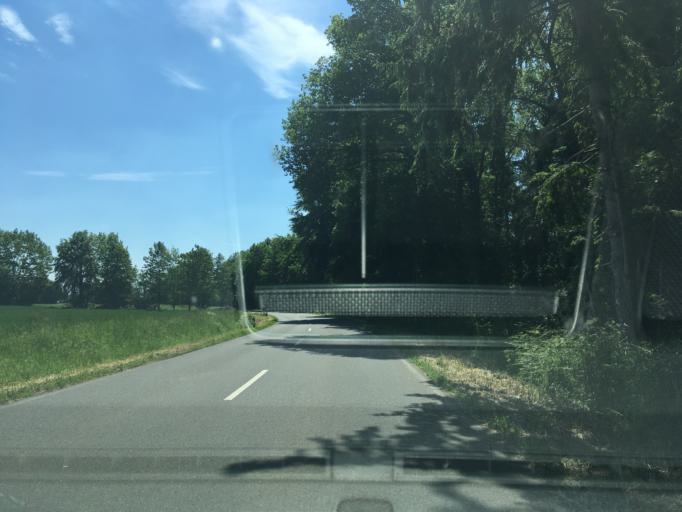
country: DE
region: North Rhine-Westphalia
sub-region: Regierungsbezirk Munster
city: Borken
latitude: 51.8865
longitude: 6.8195
